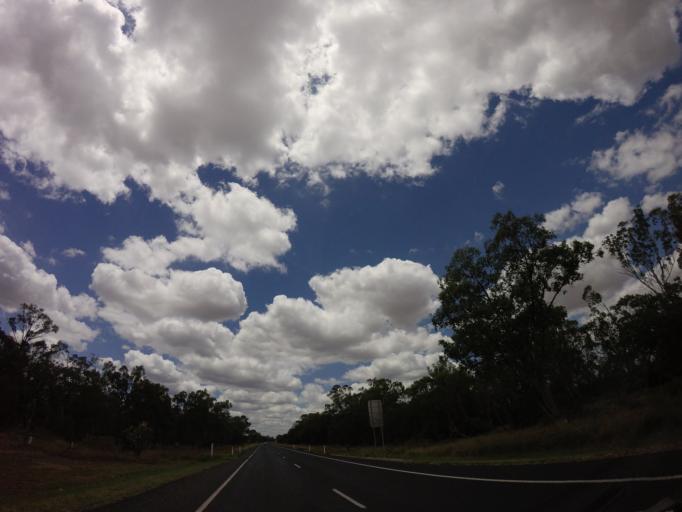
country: AU
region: Queensland
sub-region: Goondiwindi
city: Goondiwindi
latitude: -28.0765
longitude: 150.7442
